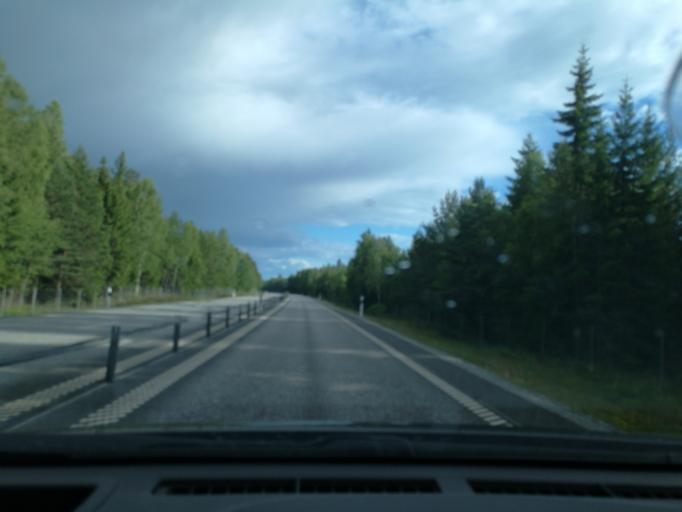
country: SE
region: Vaestmanland
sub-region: Surahammars Kommun
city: Surahammar
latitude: 59.7329
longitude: 16.2296
